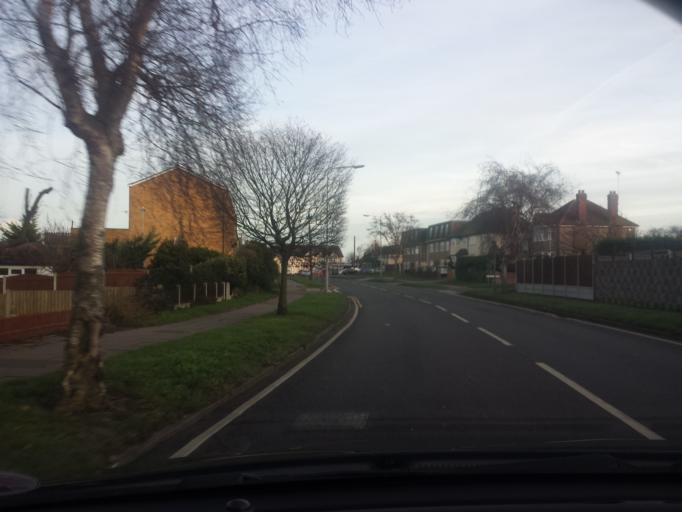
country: GB
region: England
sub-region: Essex
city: Clacton-on-Sea
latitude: 51.8028
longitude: 1.1788
